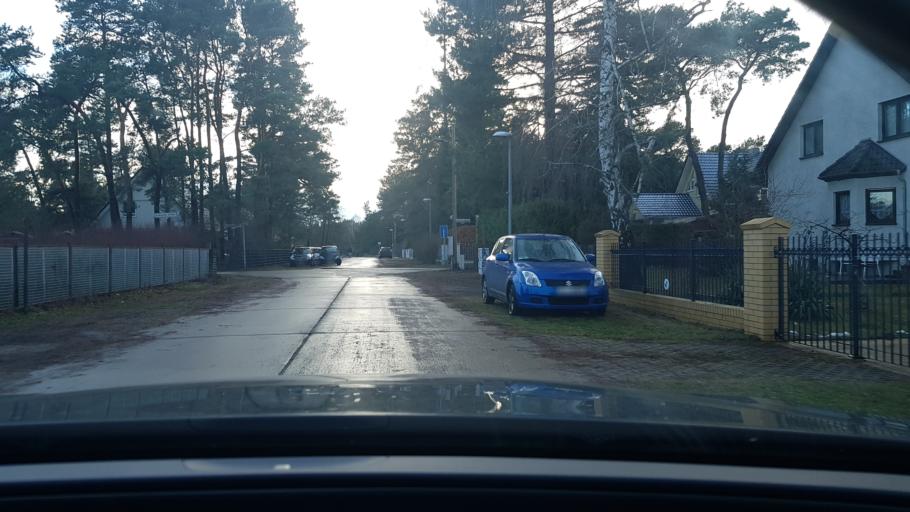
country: DE
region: Berlin
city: Muggelheim
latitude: 52.4204
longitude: 13.6685
